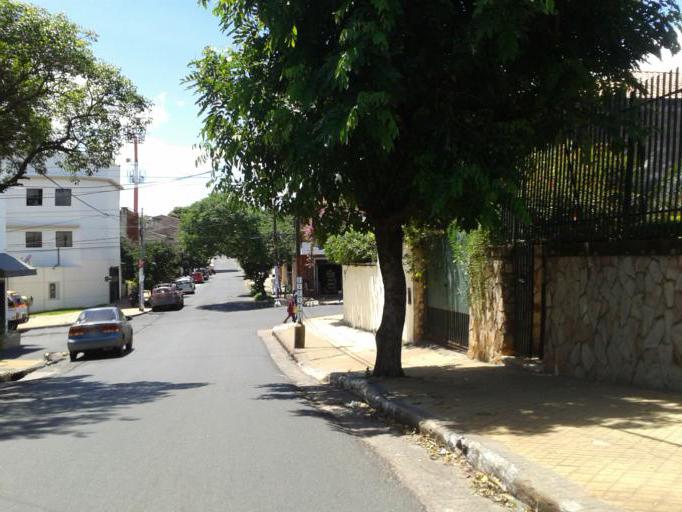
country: PY
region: Asuncion
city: Asuncion
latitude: -25.2955
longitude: -57.6178
